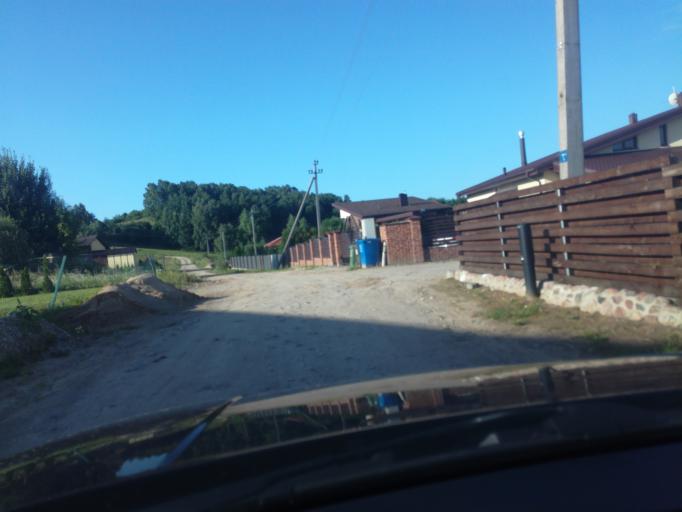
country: LT
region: Alytaus apskritis
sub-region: Alytus
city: Alytus
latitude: 54.4036
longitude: 23.9961
